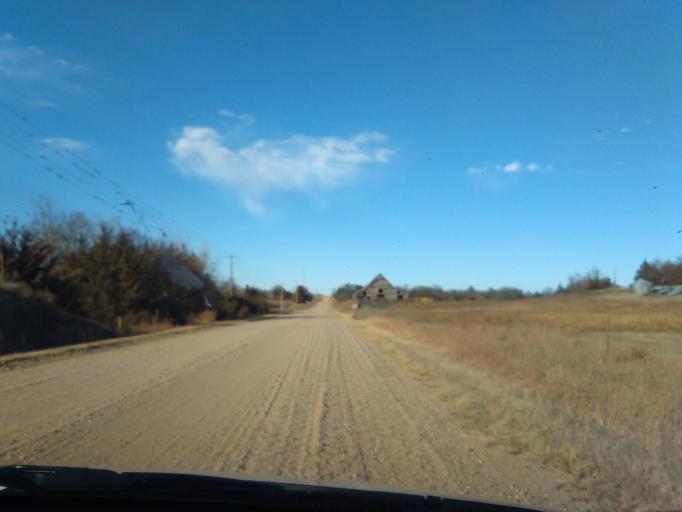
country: US
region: Nebraska
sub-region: Franklin County
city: Franklin
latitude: 40.2949
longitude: -98.7457
